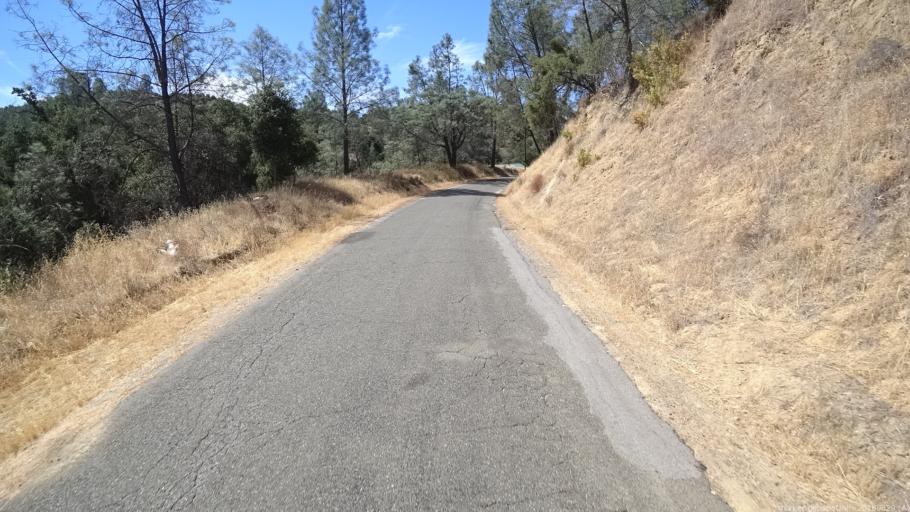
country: US
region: California
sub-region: San Luis Obispo County
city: Lake Nacimiento
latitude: 35.8222
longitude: -121.0684
